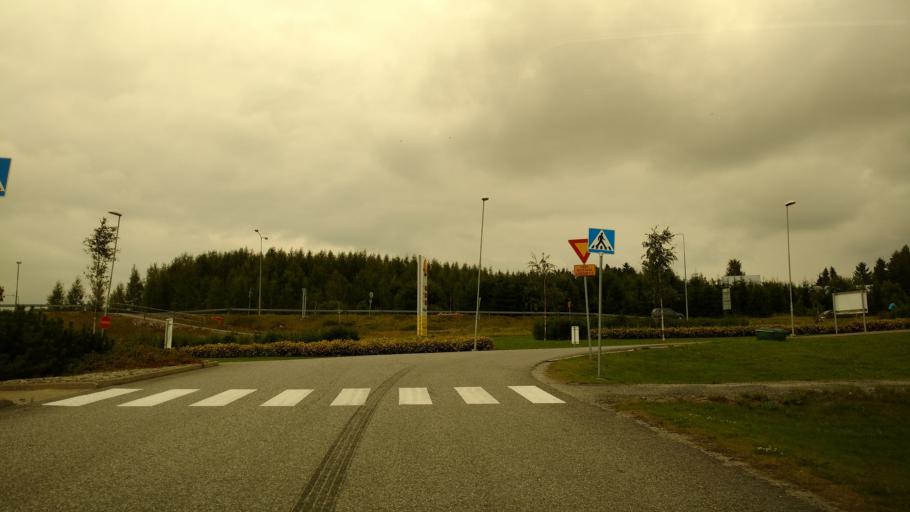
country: FI
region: Varsinais-Suomi
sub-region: Salo
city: Halikko
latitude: 60.4246
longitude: 23.0455
